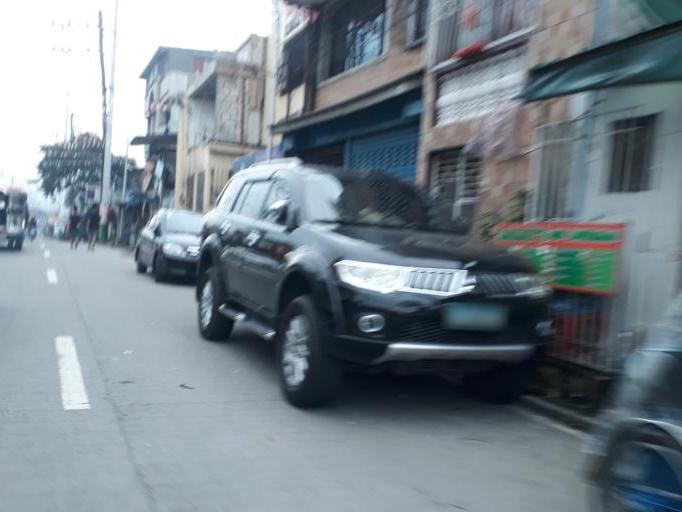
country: PH
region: Metro Manila
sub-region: Caloocan City
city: Niugan
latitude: 14.6646
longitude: 120.9675
